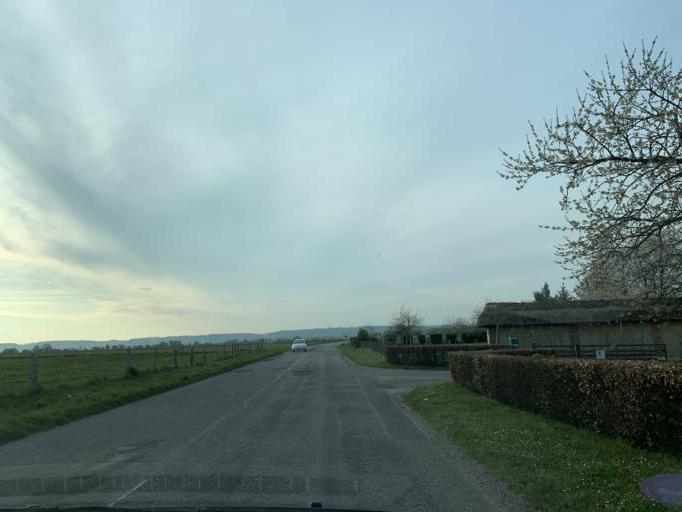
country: FR
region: Haute-Normandie
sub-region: Departement de la Seine-Maritime
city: La Mailleraye-sur-Seine
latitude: 49.4980
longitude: 0.7564
